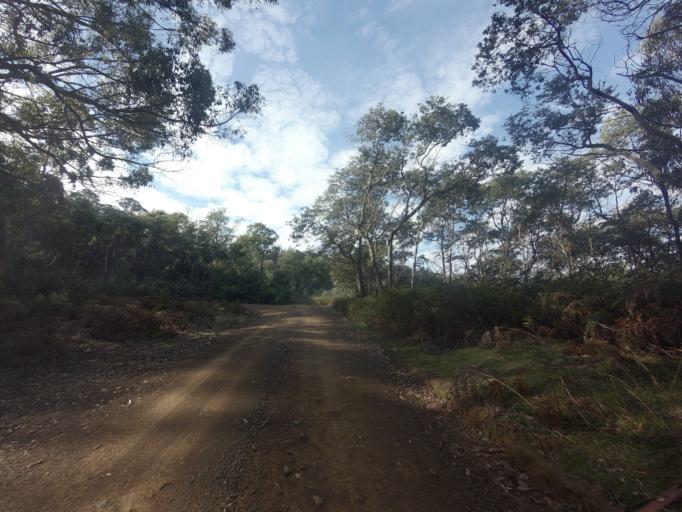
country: AU
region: Tasmania
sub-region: Sorell
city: Sorell
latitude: -42.5263
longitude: 147.4642
